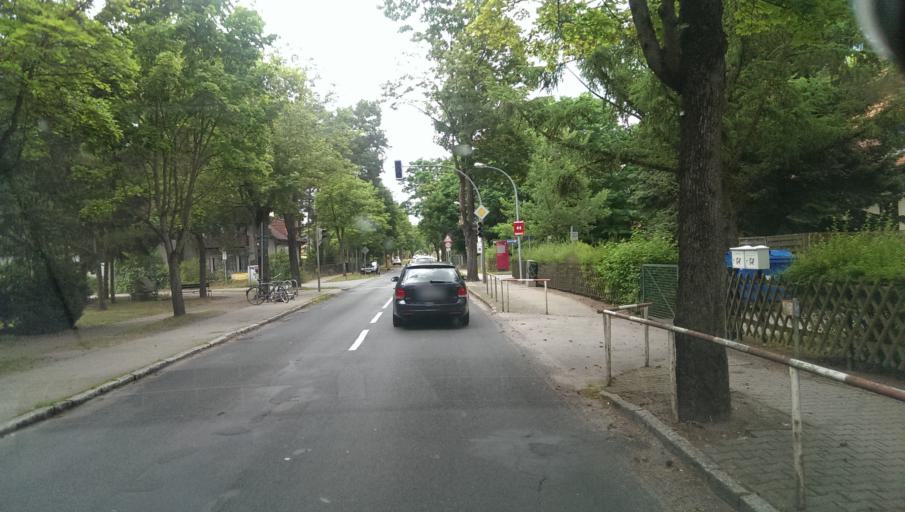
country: DE
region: Brandenburg
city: Fichtenwalde
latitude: 52.2803
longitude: 12.8899
